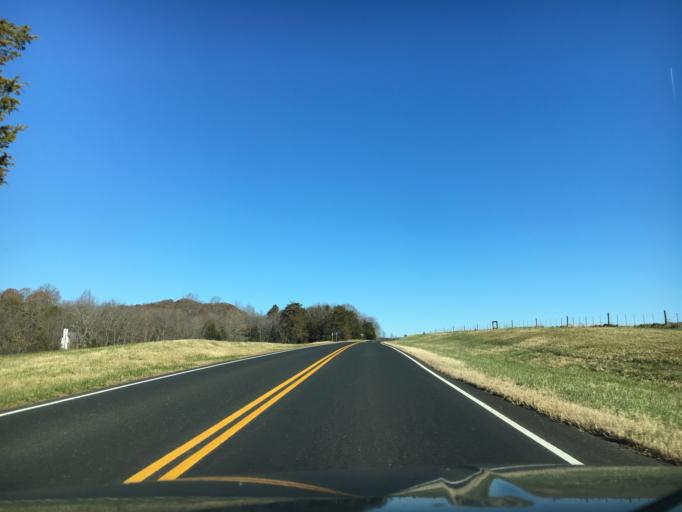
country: US
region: Virginia
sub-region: Appomattox County
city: Appomattox
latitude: 37.3840
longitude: -78.7889
